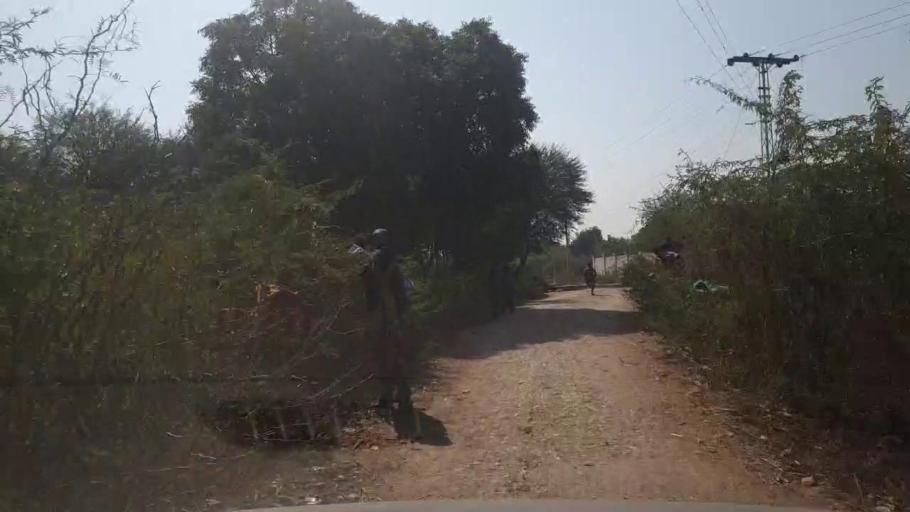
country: PK
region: Sindh
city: Chambar
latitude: 25.2596
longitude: 68.8338
